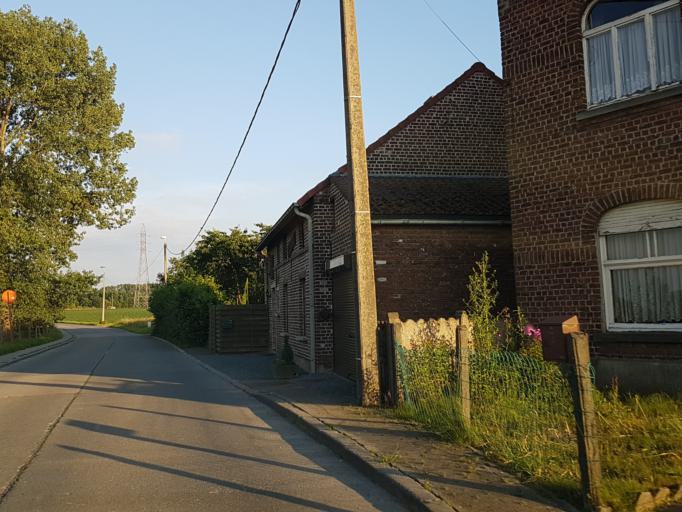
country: BE
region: Flanders
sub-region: Provincie Vlaams-Brabant
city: Ternat
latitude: 50.8667
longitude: 4.1850
